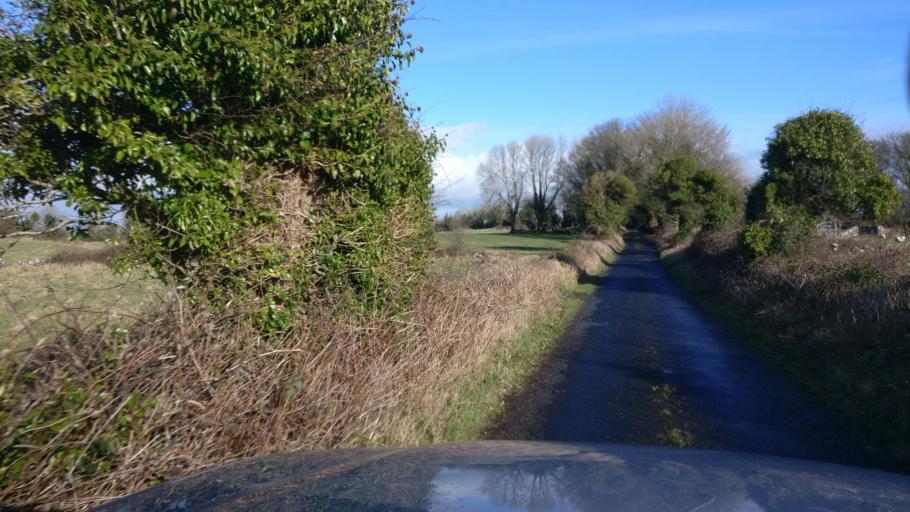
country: IE
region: Connaught
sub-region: County Galway
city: Loughrea
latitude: 53.2146
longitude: -8.6682
